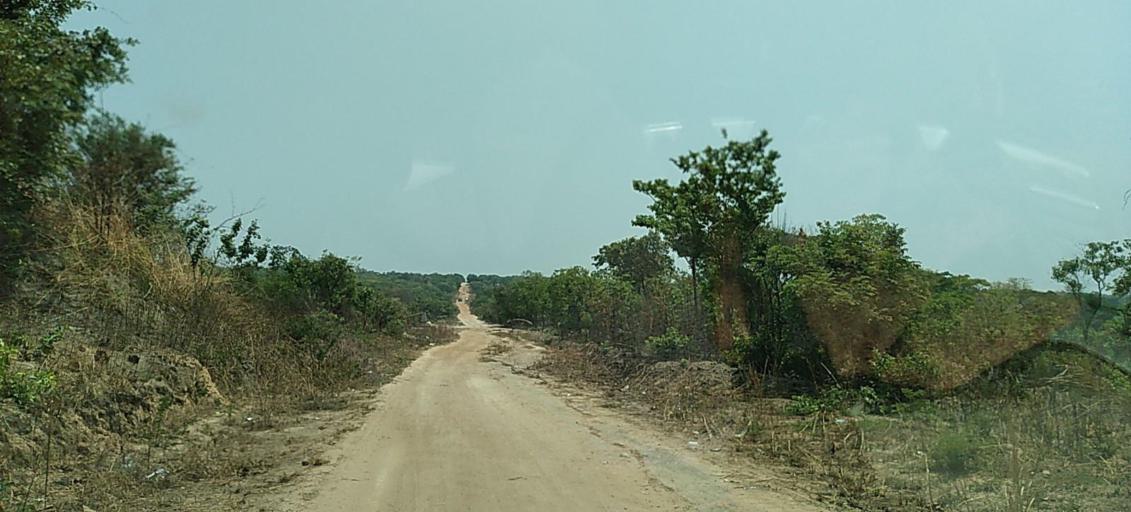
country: ZM
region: Copperbelt
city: Kalulushi
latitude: -12.9350
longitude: 28.1627
